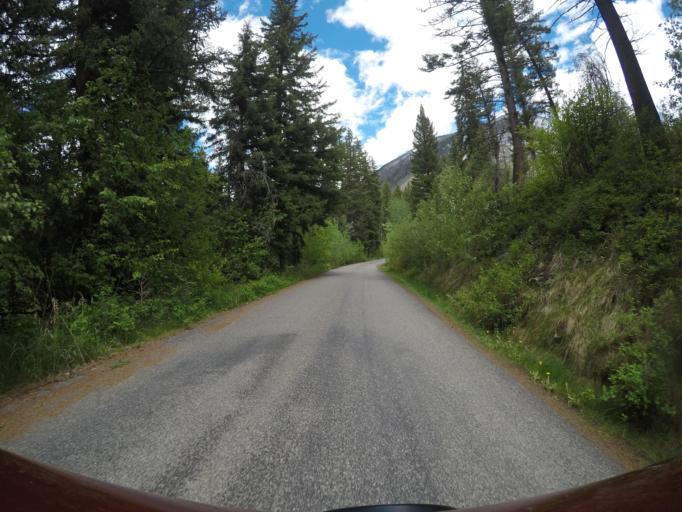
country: US
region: Montana
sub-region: Park County
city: Livingston
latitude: 45.4980
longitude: -110.5274
